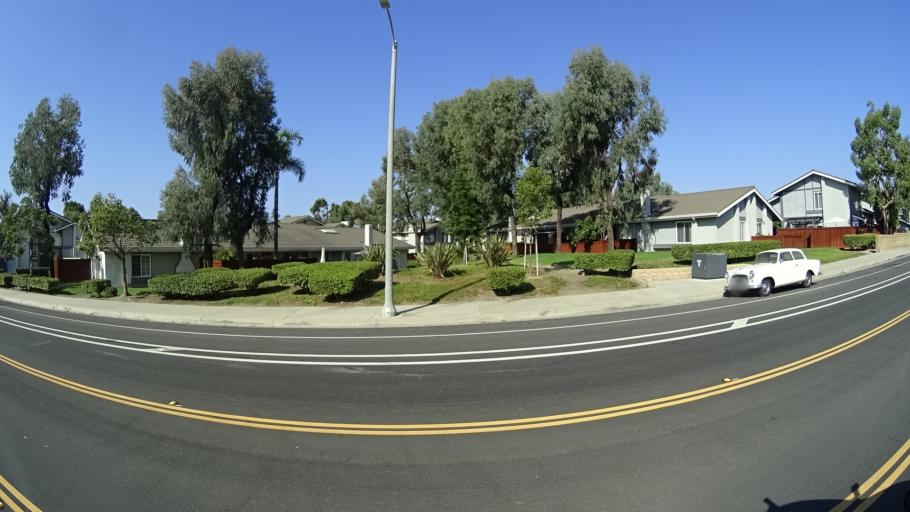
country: US
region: California
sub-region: Orange County
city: San Clemente
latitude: 33.4515
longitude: -117.6520
